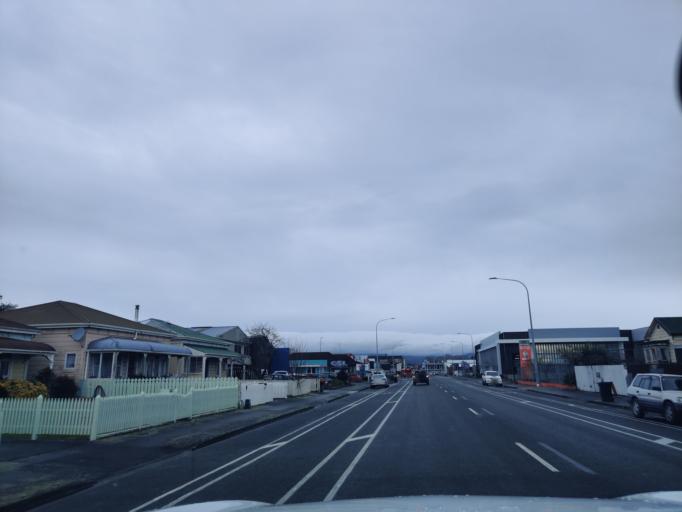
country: NZ
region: Manawatu-Wanganui
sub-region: Palmerston North City
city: Palmerston North
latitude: -40.3541
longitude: 175.6032
